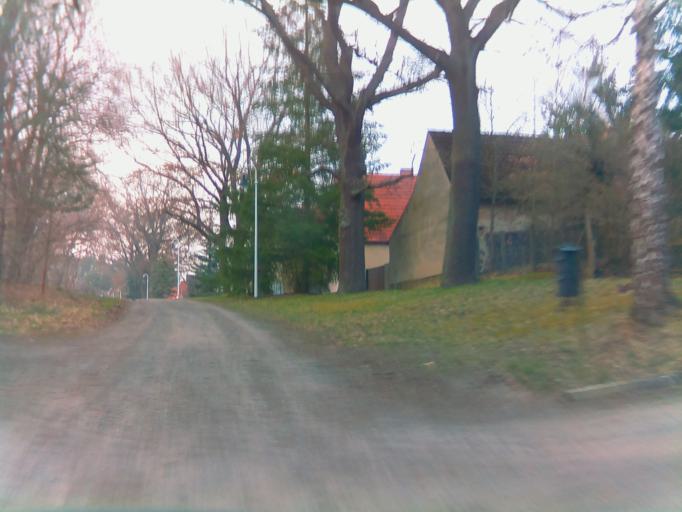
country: DE
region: Brandenburg
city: Jamlitz
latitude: 51.9826
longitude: 14.4097
